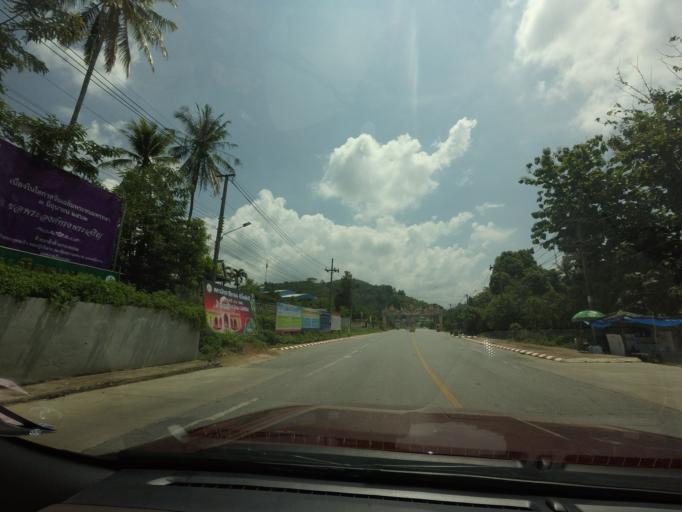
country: TH
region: Yala
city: Betong
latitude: 5.7853
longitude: 101.0727
